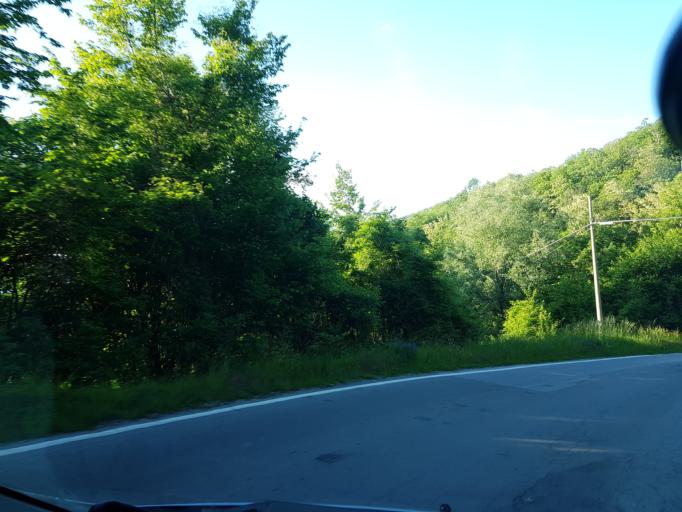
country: IT
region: Tuscany
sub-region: Provincia di Lucca
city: Minucciano
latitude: 44.1657
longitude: 10.2100
